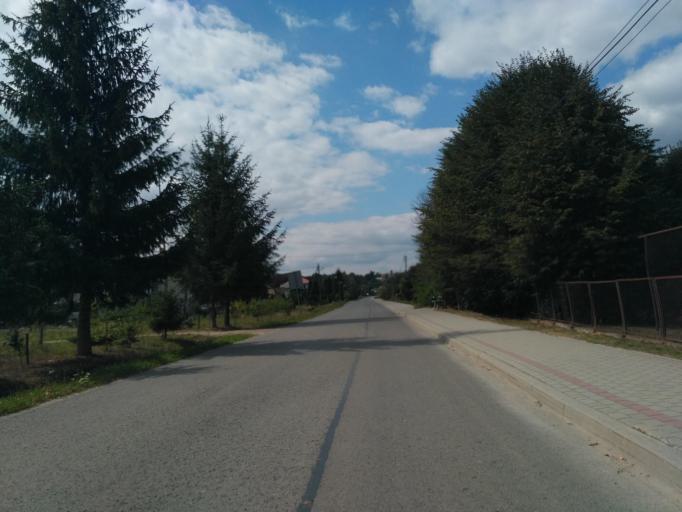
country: PL
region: Subcarpathian Voivodeship
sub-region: Powiat rzeszowski
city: Dynow
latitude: 49.8149
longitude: 22.2852
